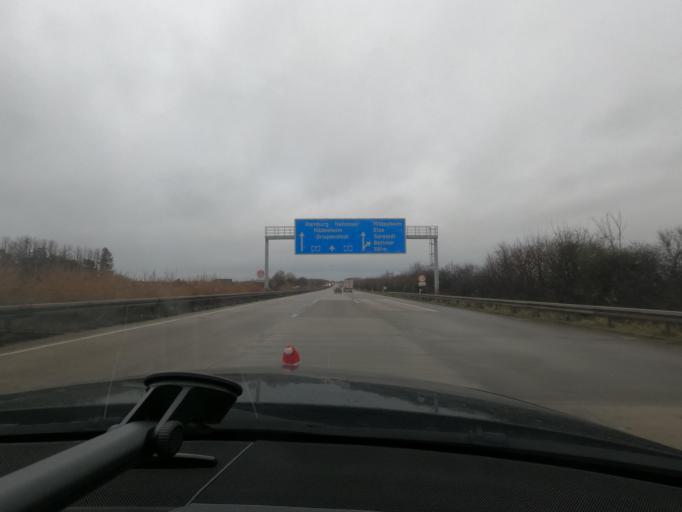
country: DE
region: Lower Saxony
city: Hildesheim
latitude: 52.1523
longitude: 9.9920
